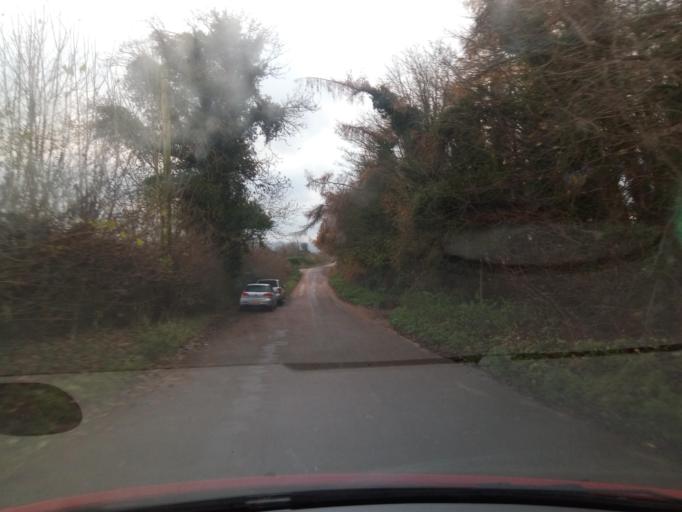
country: GB
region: Scotland
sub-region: The Scottish Borders
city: Newtown St Boswells
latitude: 55.5879
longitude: -2.6831
